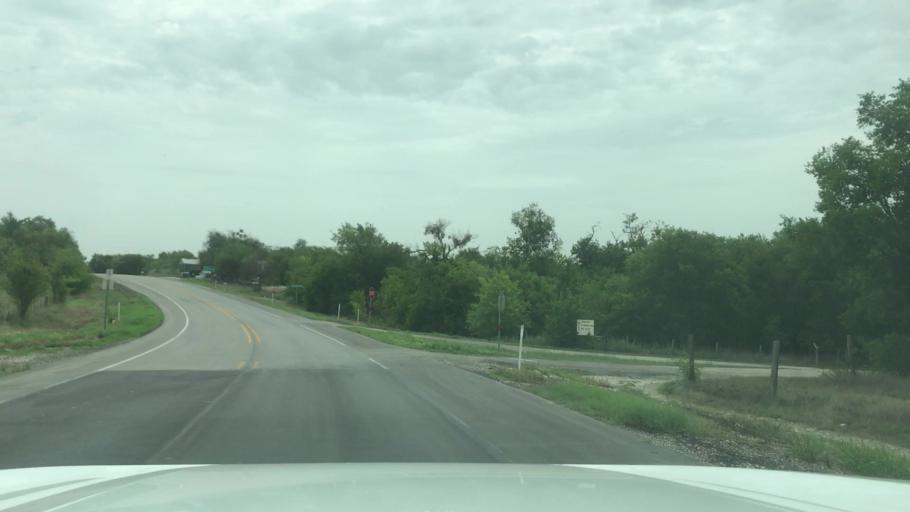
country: US
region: Texas
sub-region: Erath County
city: Dublin
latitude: 32.0598
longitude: -98.2106
